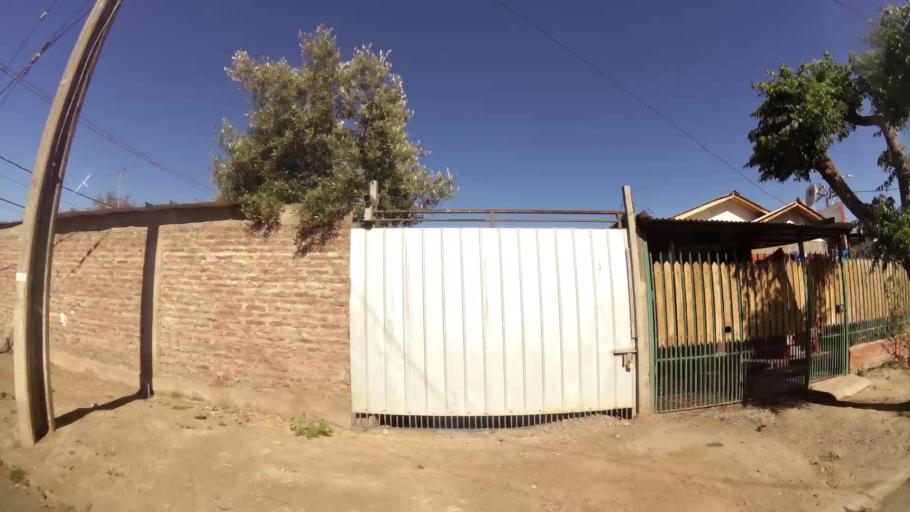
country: CL
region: Santiago Metropolitan
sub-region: Provincia de Santiago
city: La Pintana
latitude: -33.5874
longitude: -70.6656
